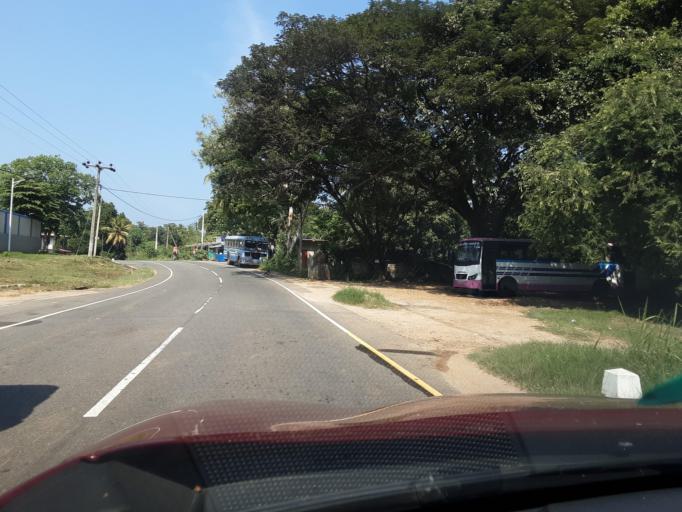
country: LK
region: Uva
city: Badulla
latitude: 7.1864
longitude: 81.0404
